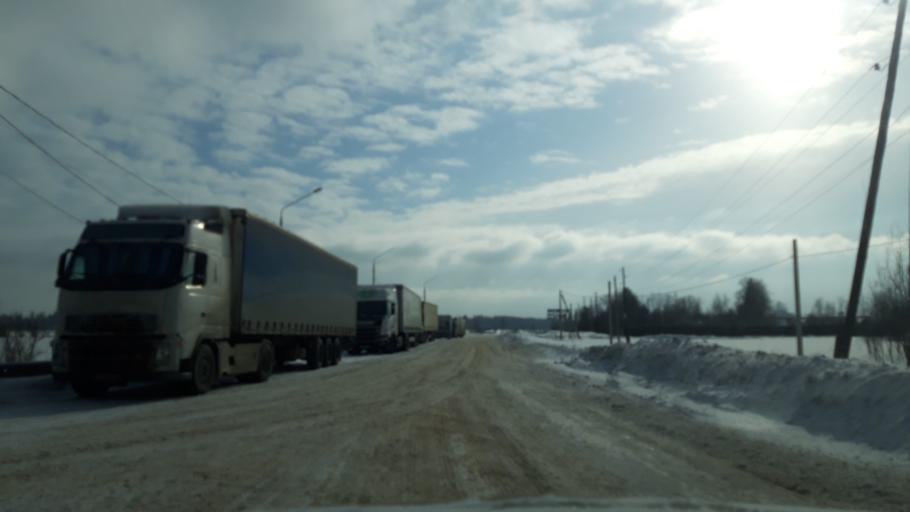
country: RU
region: Moskovskaya
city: Yermolino
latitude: 56.1417
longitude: 37.3799
